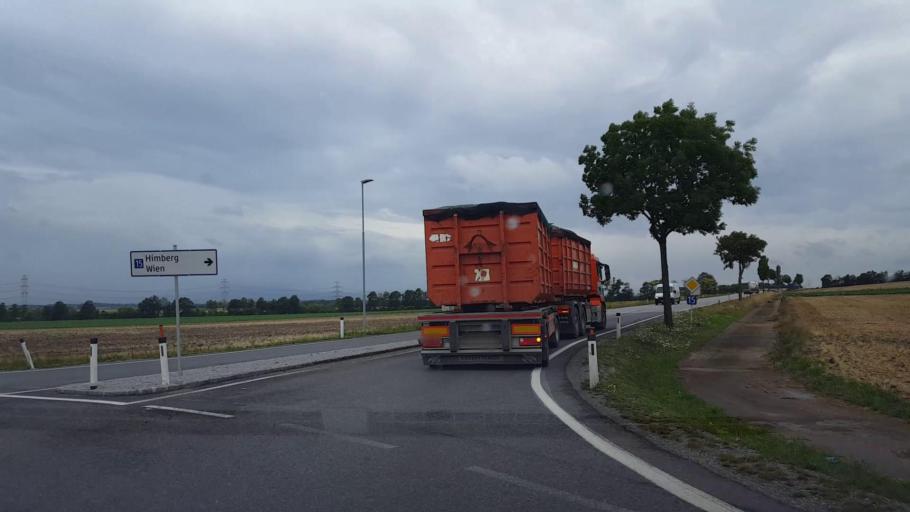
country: AT
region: Lower Austria
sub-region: Politischer Bezirk Wien-Umgebung
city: Ebergassing
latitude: 48.0540
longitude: 16.5049
